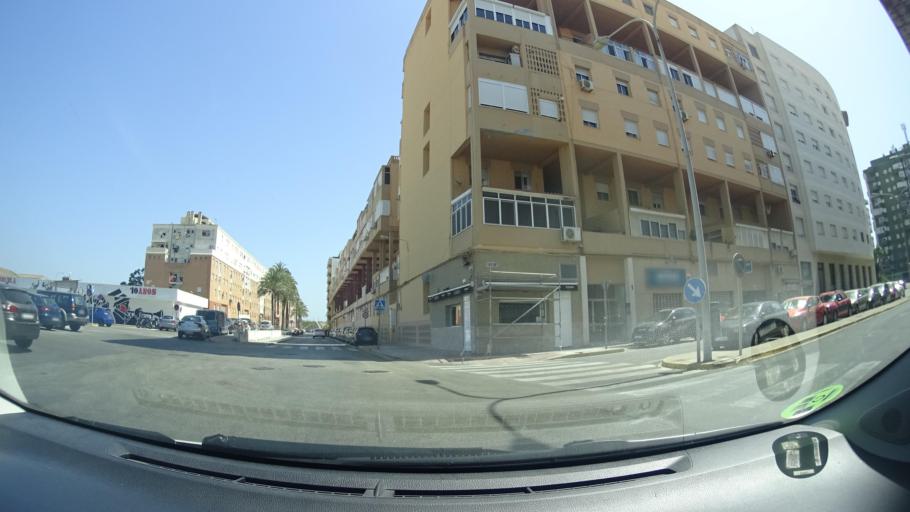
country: ES
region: Andalusia
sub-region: Provincia de Cadiz
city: Cadiz
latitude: 36.4977
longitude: -6.2705
